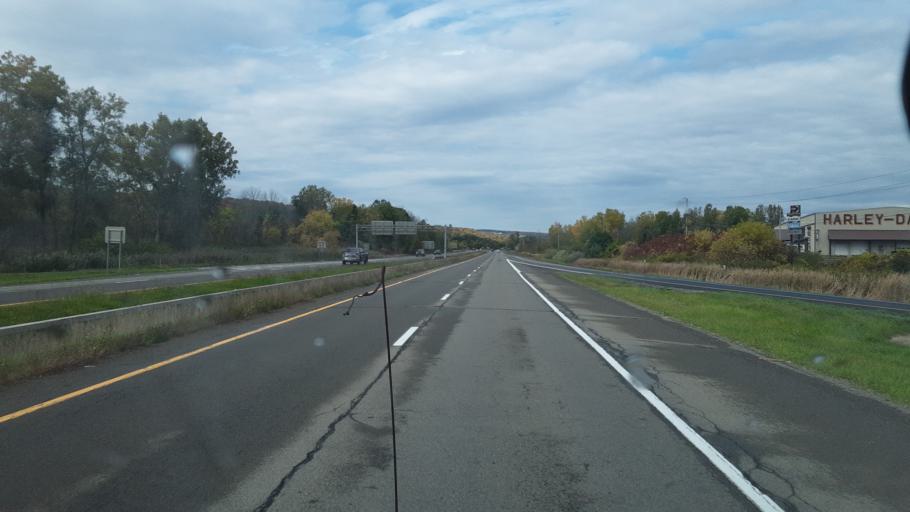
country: US
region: New York
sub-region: Steuben County
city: Hornell
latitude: 42.3729
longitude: -77.6805
